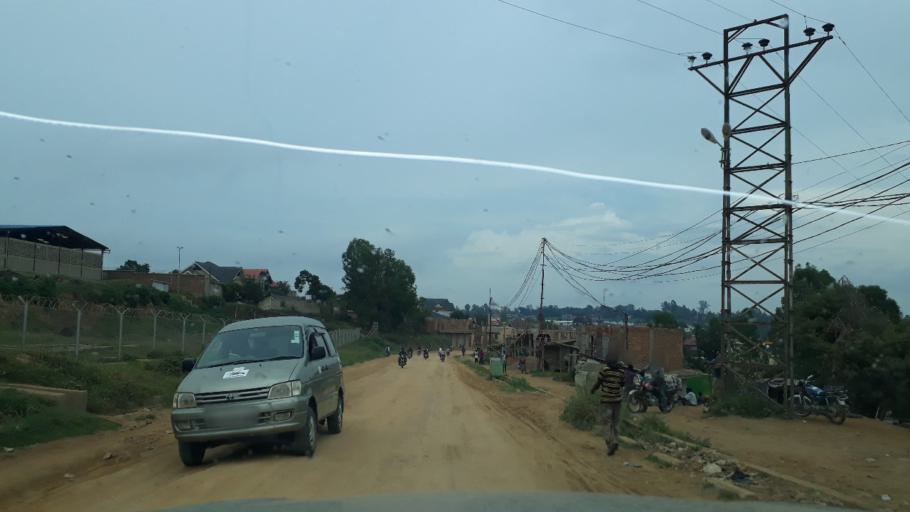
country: CD
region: Eastern Province
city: Bunia
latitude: 1.5742
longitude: 30.2475
